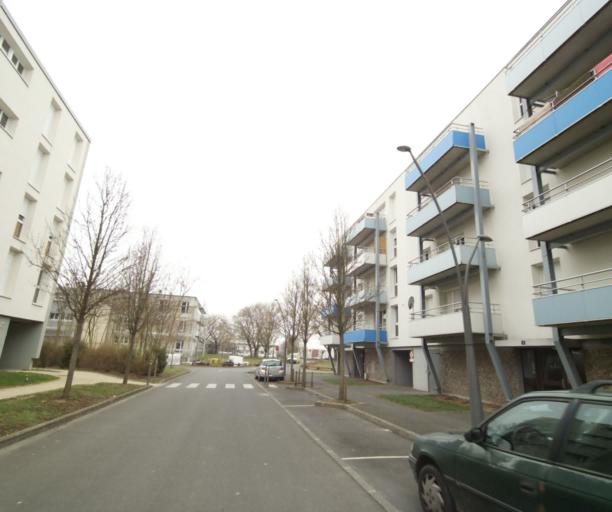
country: FR
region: Poitou-Charentes
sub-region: Departement des Deux-Sevres
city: Niort
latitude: 46.3151
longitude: -0.4842
